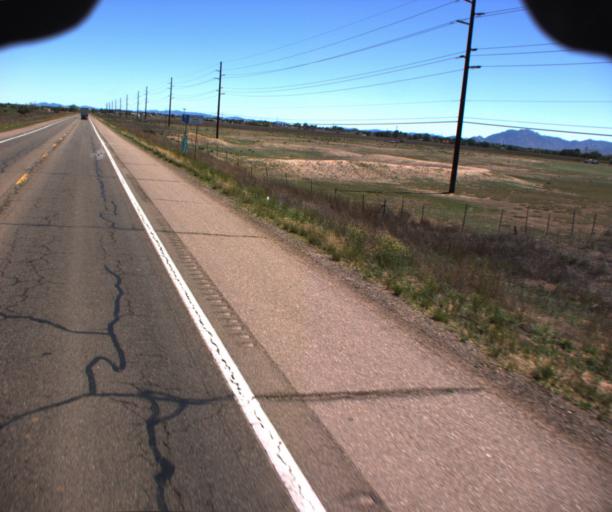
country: US
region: Arizona
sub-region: Yavapai County
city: Chino Valley
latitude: 34.8152
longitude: -112.4535
